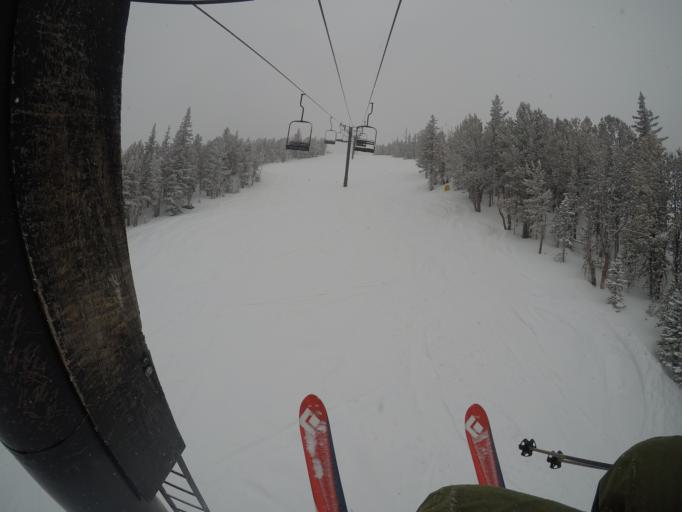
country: US
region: Montana
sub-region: Carbon County
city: Red Lodge
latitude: 45.1827
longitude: -109.3545
